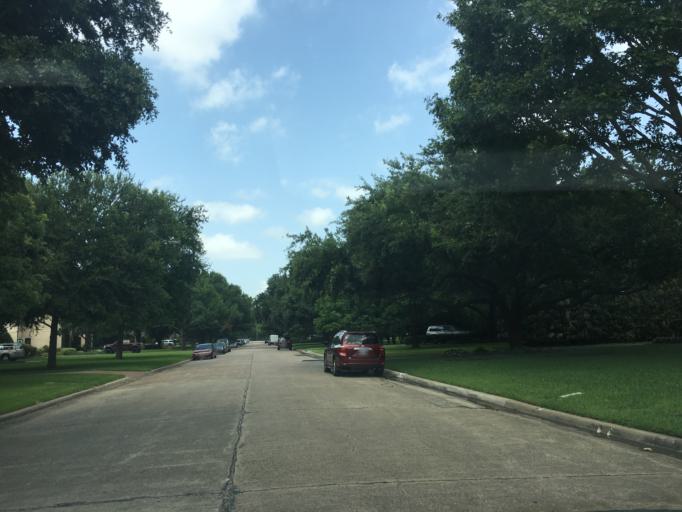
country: US
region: Texas
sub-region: Dallas County
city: University Park
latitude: 32.8722
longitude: -96.8000
